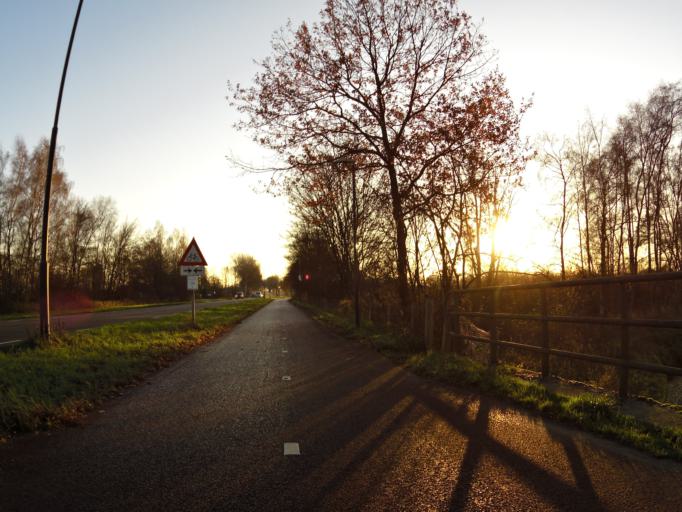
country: NL
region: North Brabant
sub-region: Gemeente Vught
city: Vught
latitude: 51.6491
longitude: 5.3196
